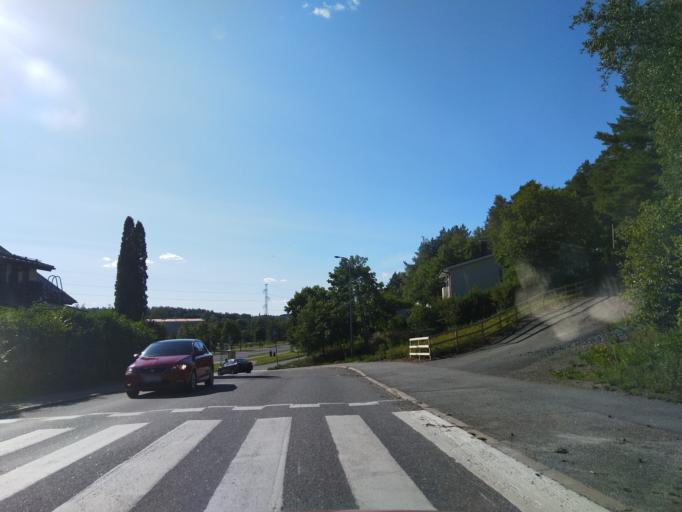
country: FI
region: Varsinais-Suomi
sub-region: Turku
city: Kaarina
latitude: 60.4438
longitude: 22.3345
